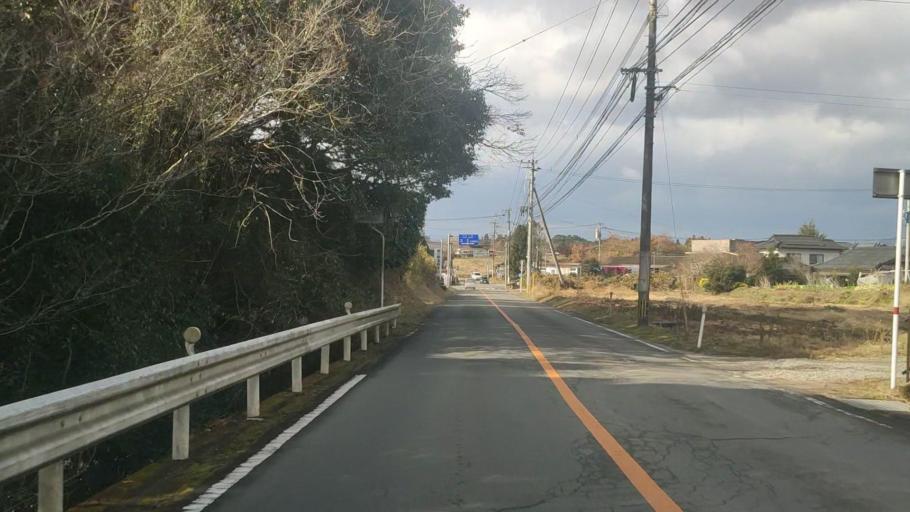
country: JP
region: Kumamoto
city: Hitoyoshi
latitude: 32.2356
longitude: 130.7918
